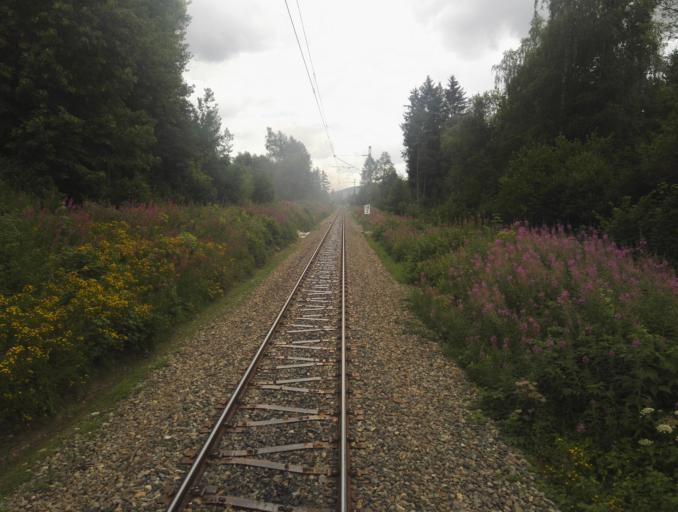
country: DE
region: Baden-Wuerttemberg
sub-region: Freiburg Region
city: Schluchsee
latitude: 47.8285
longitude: 8.1433
